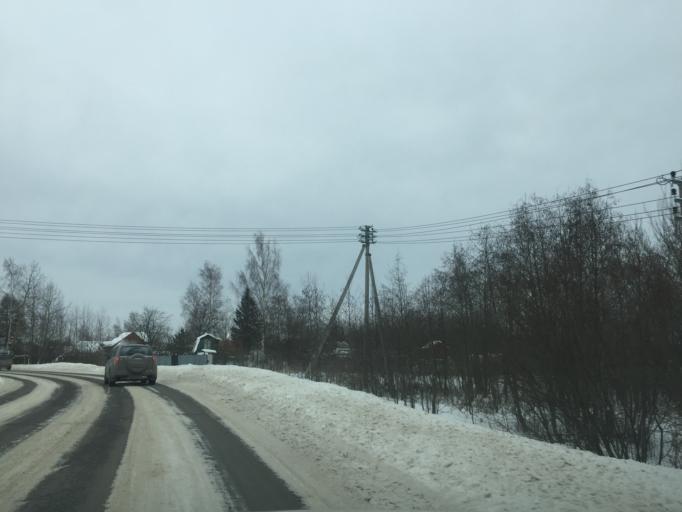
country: RU
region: Leningrad
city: Imeni Sverdlova
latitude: 59.7874
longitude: 30.7118
